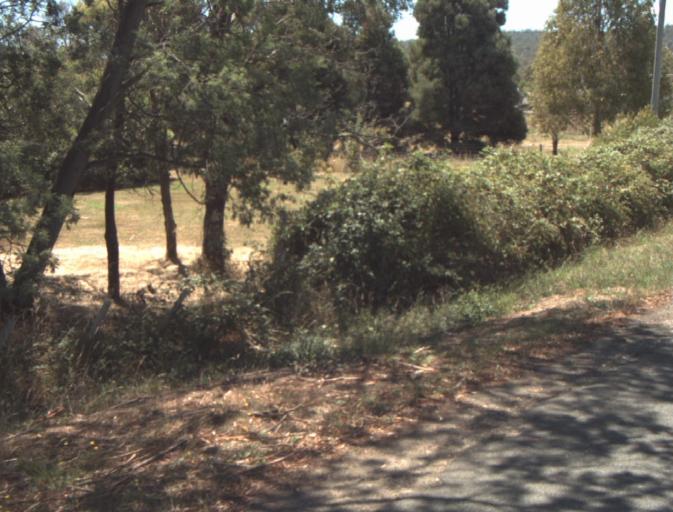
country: AU
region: Tasmania
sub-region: Launceston
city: Mayfield
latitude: -41.3719
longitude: 147.1380
